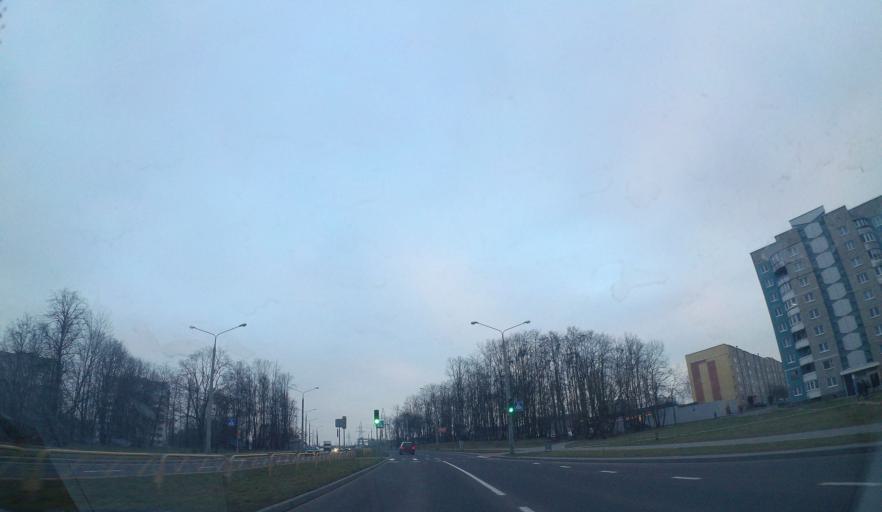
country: BY
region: Grodnenskaya
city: Hrodna
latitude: 53.6564
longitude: 23.7832
